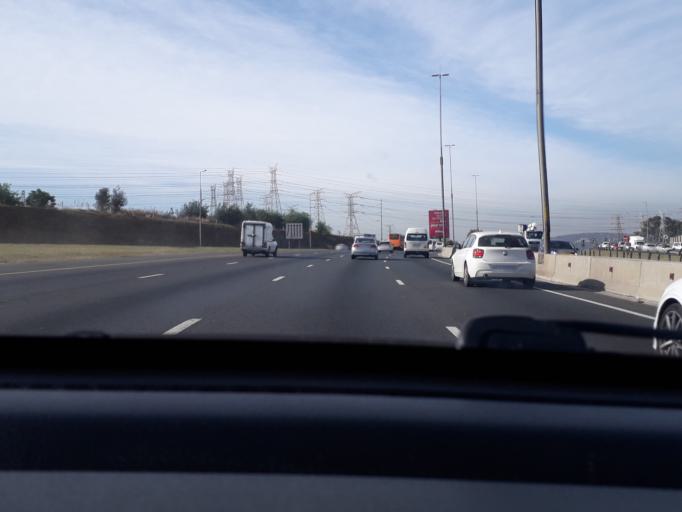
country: ZA
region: Gauteng
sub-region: City of Johannesburg Metropolitan Municipality
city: Modderfontein
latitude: -26.1237
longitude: 28.1363
